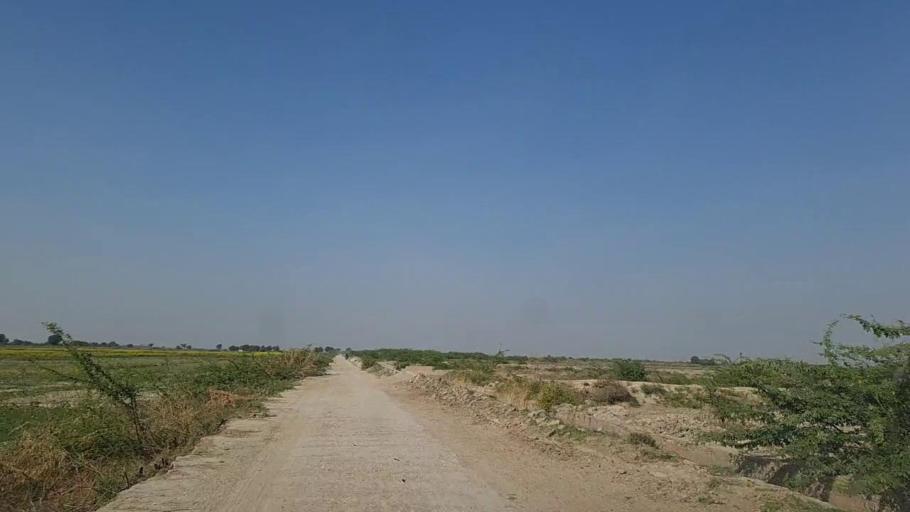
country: PK
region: Sindh
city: Naukot
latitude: 24.8996
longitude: 69.4875
